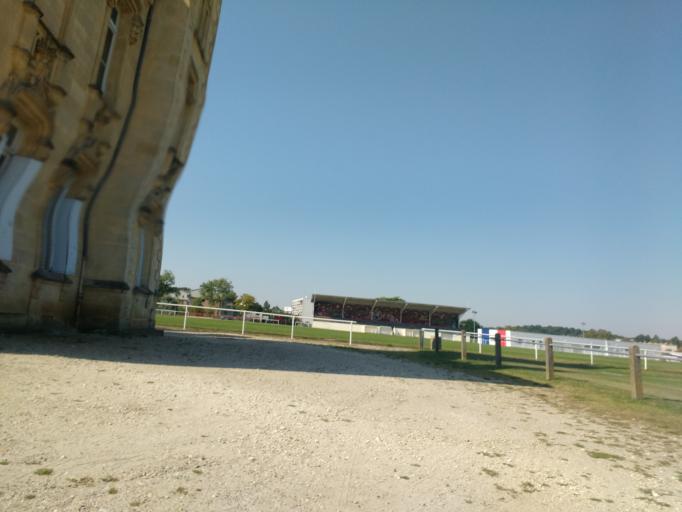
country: FR
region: Aquitaine
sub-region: Departement de la Gironde
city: Pessac
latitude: 44.8124
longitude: -0.6296
